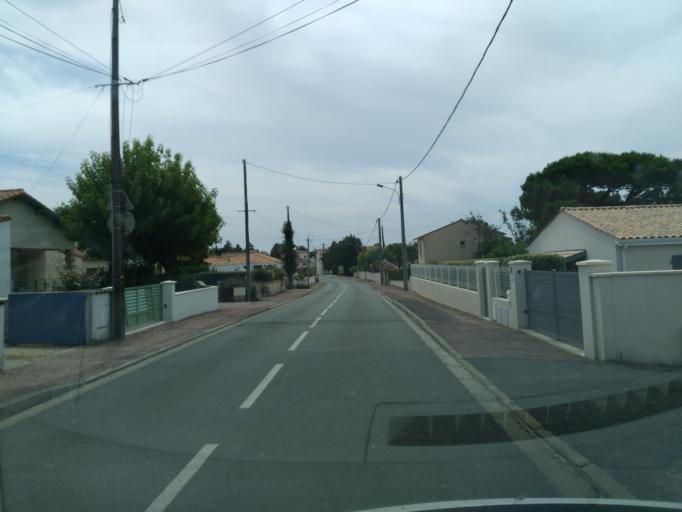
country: FR
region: Poitou-Charentes
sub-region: Departement de la Charente-Maritime
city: Saint-Palais-sur-Mer
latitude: 45.6587
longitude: -1.0758
